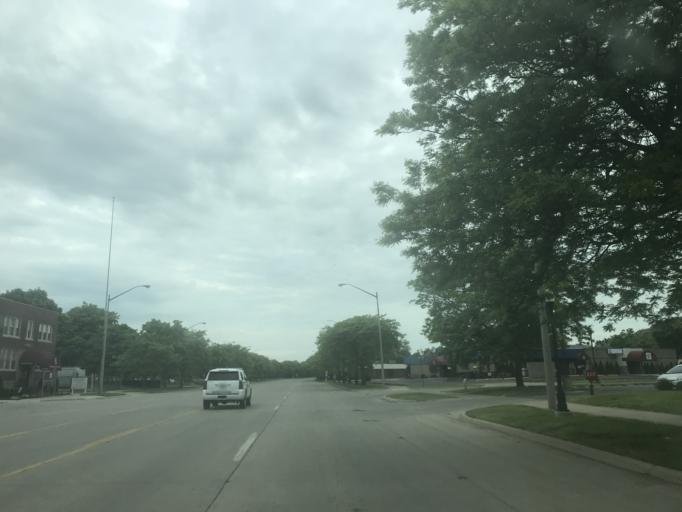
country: US
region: Michigan
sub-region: Wayne County
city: Wyandotte
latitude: 42.1984
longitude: -83.1516
